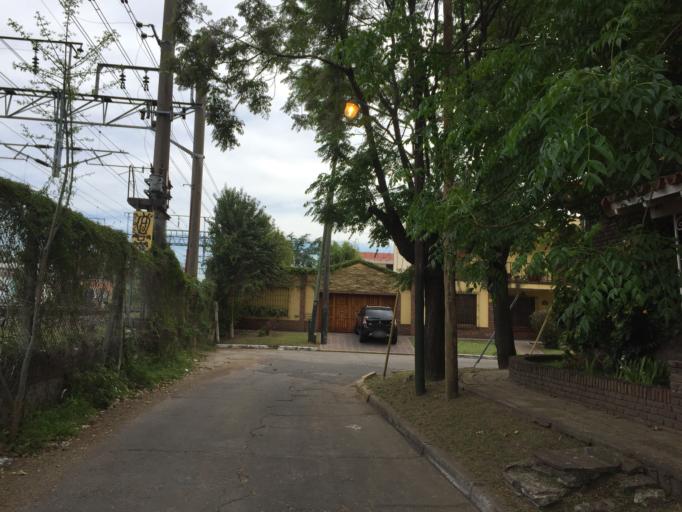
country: AR
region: Buenos Aires
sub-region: Partido de Lomas de Zamora
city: Lomas de Zamora
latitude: -34.7541
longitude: -58.3964
